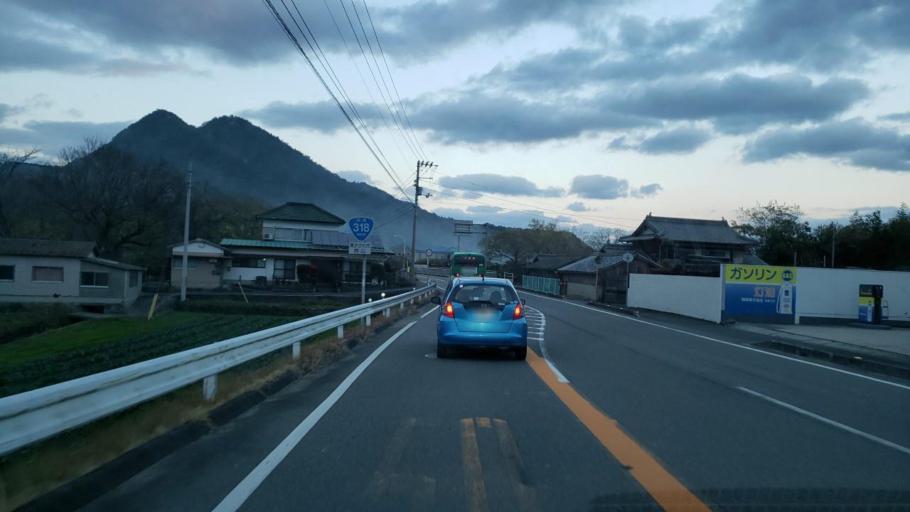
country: JP
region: Tokushima
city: Kamojimacho-jogejima
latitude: 34.2101
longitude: 134.3312
